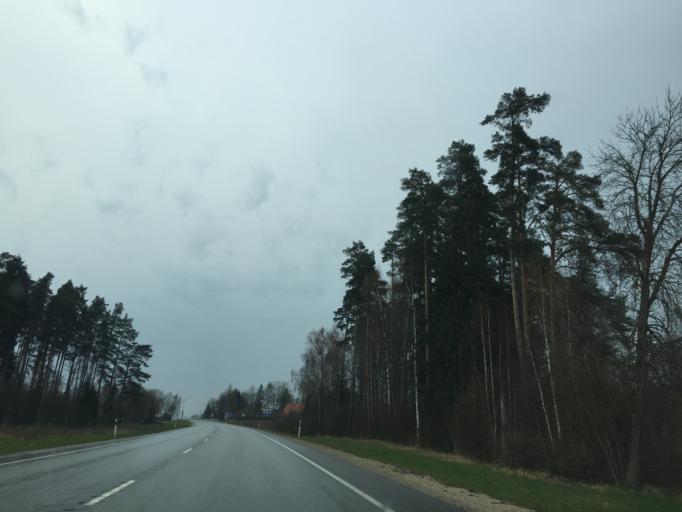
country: EE
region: Tartu
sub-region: UElenurme vald
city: Ulenurme
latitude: 58.2266
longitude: 26.6995
